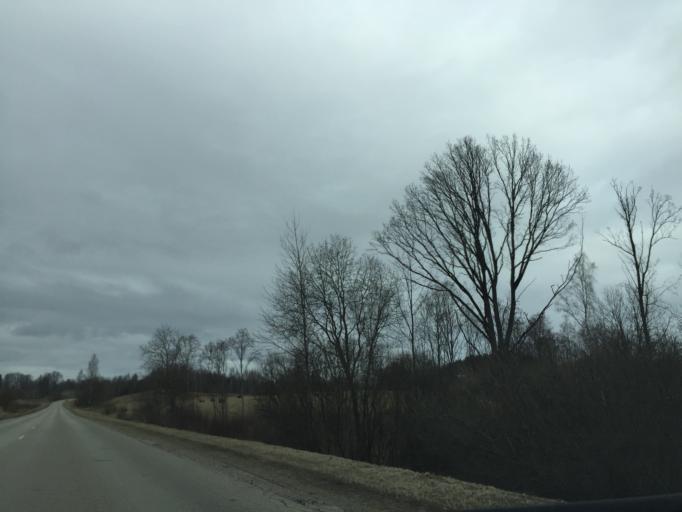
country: LV
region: Kraslavas Rajons
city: Kraslava
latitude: 55.9519
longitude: 27.1629
